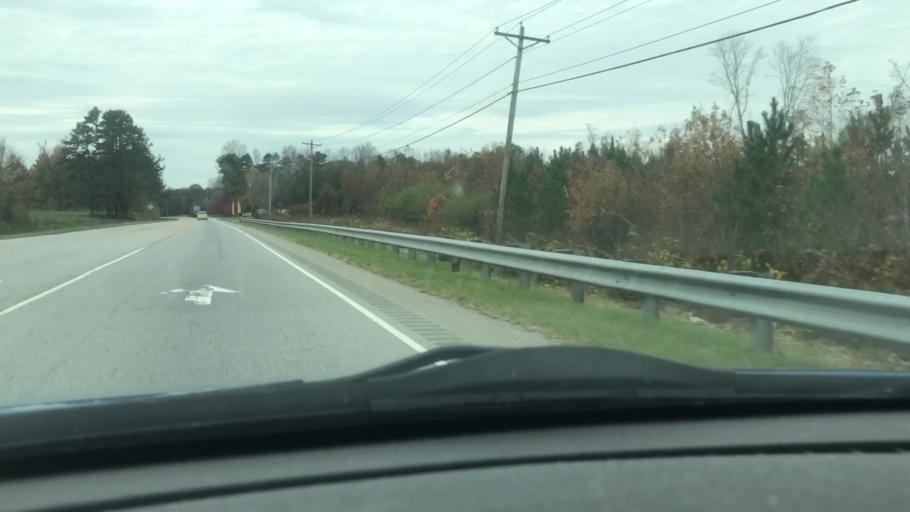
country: US
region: North Carolina
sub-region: Randolph County
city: Trinity
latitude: 35.7481
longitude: -80.0078
